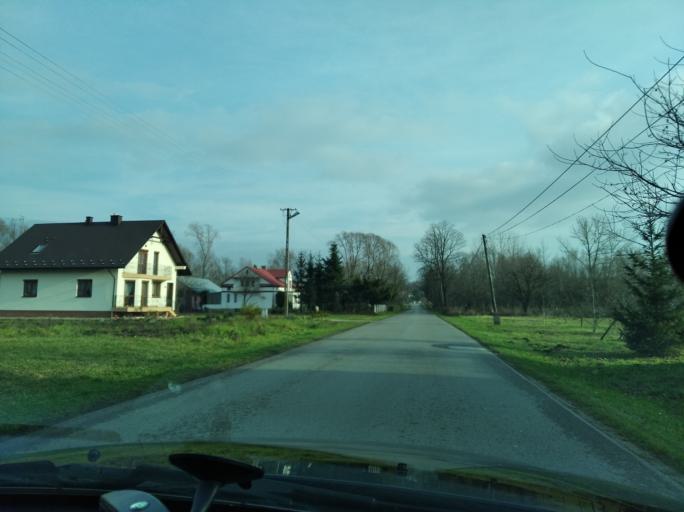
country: PL
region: Subcarpathian Voivodeship
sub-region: Powiat przeworski
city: Siedleczka
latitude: 49.9546
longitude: 22.3930
